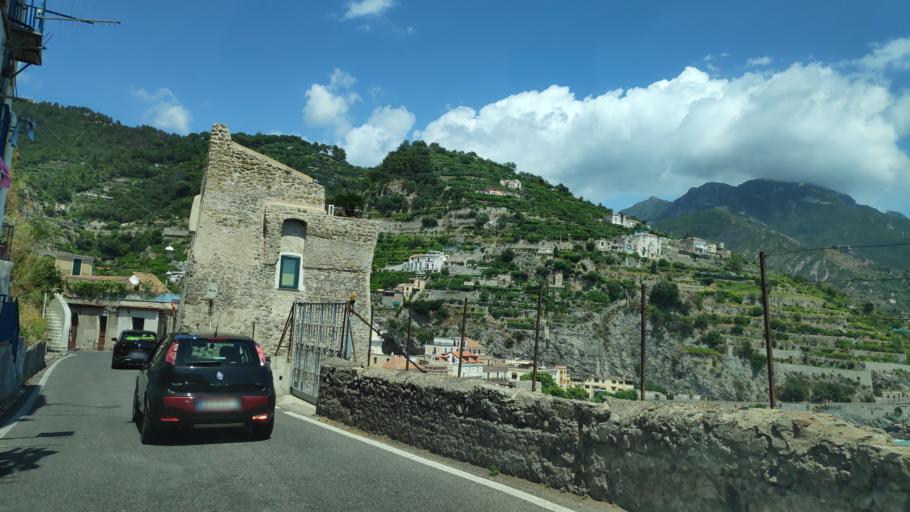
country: IT
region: Campania
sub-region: Provincia di Salerno
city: Minori
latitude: 40.6483
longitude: 14.6255
